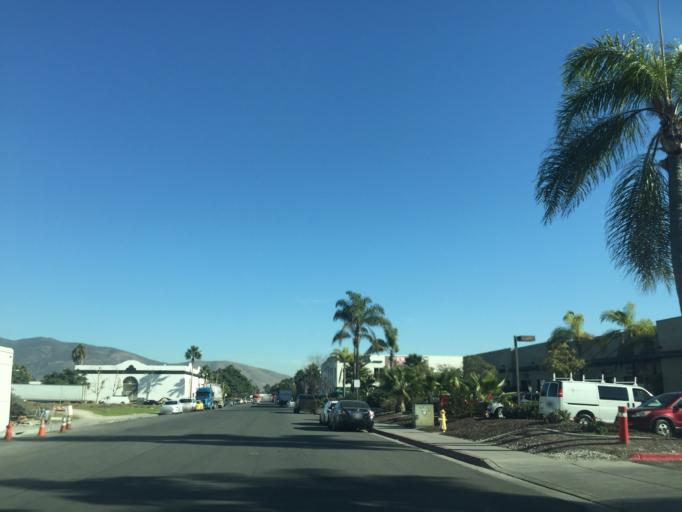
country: MX
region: Baja California
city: Tijuana
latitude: 32.5543
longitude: -116.9354
